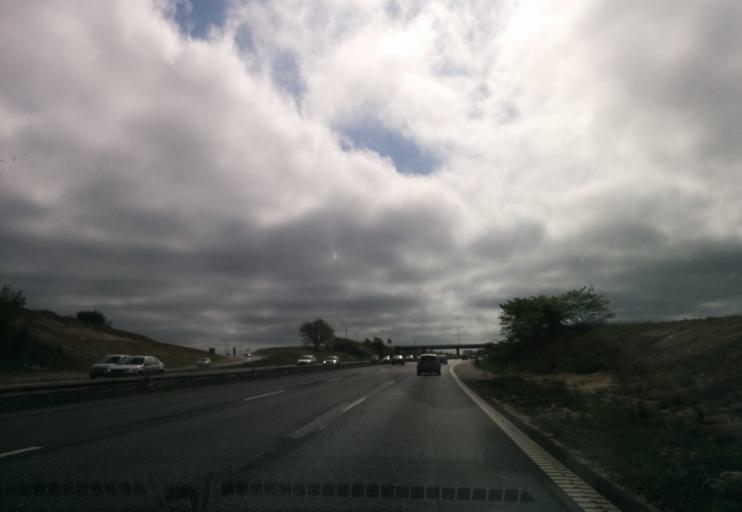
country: DK
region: South Denmark
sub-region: Middelfart Kommune
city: Strib
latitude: 55.5145
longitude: 9.7689
